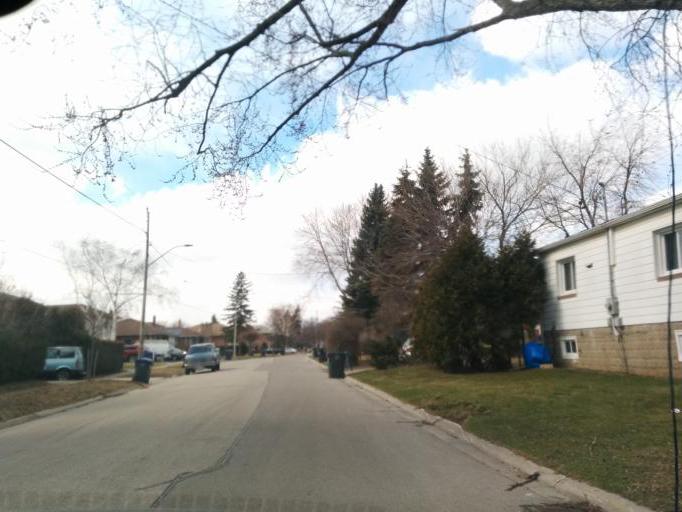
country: CA
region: Ontario
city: Etobicoke
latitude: 43.5835
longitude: -79.5664
